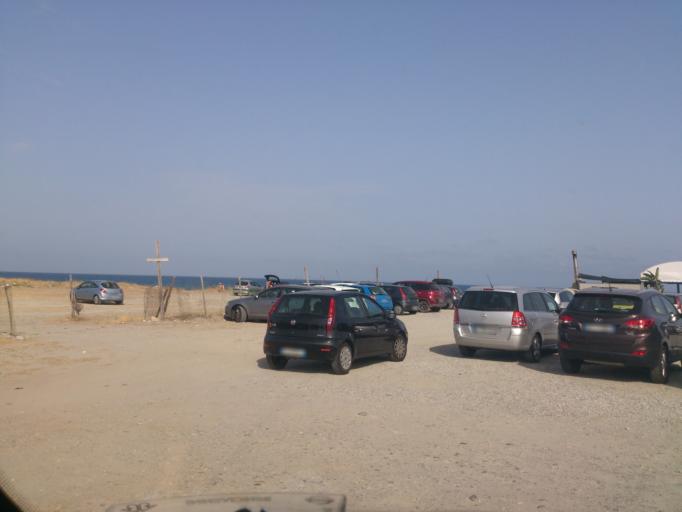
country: IT
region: Calabria
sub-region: Provincia di Reggio Calabria
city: Monasterace Marina
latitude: 38.4189
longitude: 16.5624
